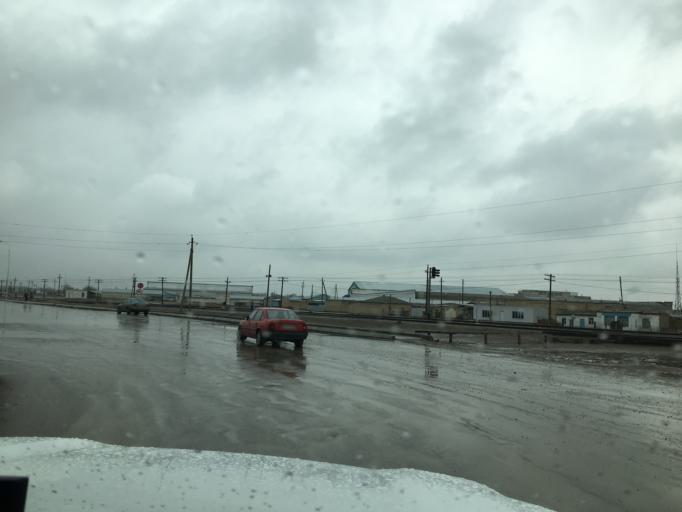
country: TM
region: Mary
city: Yoloeten
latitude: 37.2921
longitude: 62.3567
